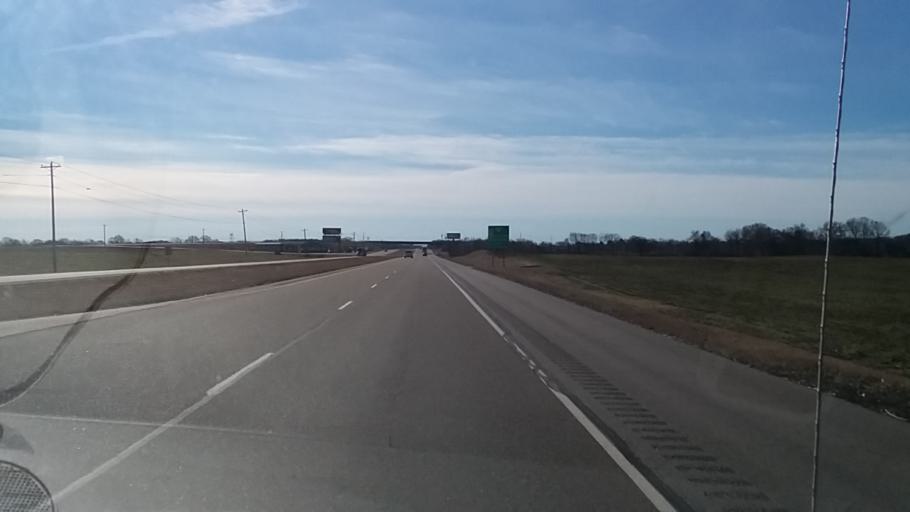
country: US
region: Tennessee
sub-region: Crockett County
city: Alamo
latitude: 35.8885
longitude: -89.2334
